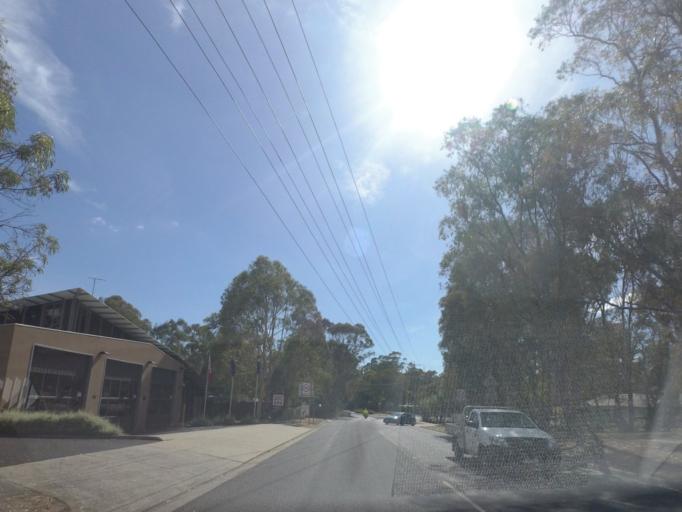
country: AU
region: Victoria
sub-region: Nillumbik
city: Hurstbridge
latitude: -37.6360
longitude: 145.1997
